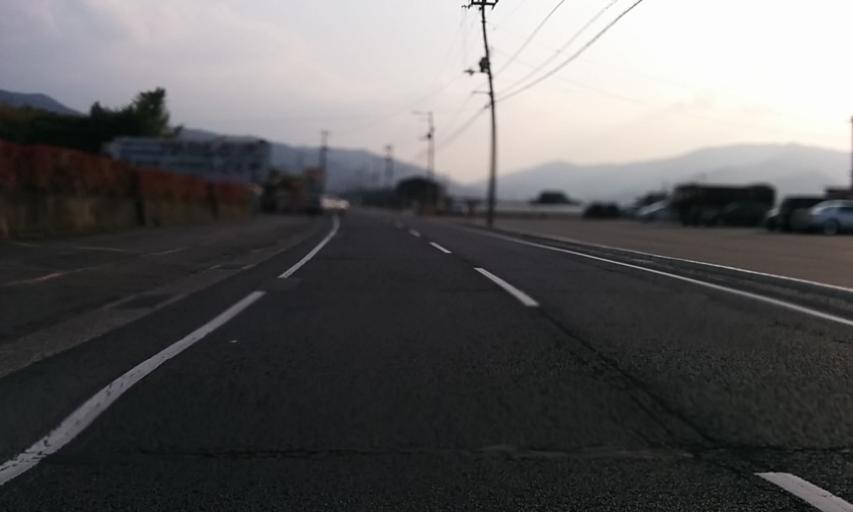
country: JP
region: Ehime
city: Saijo
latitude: 33.8765
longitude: 133.0641
